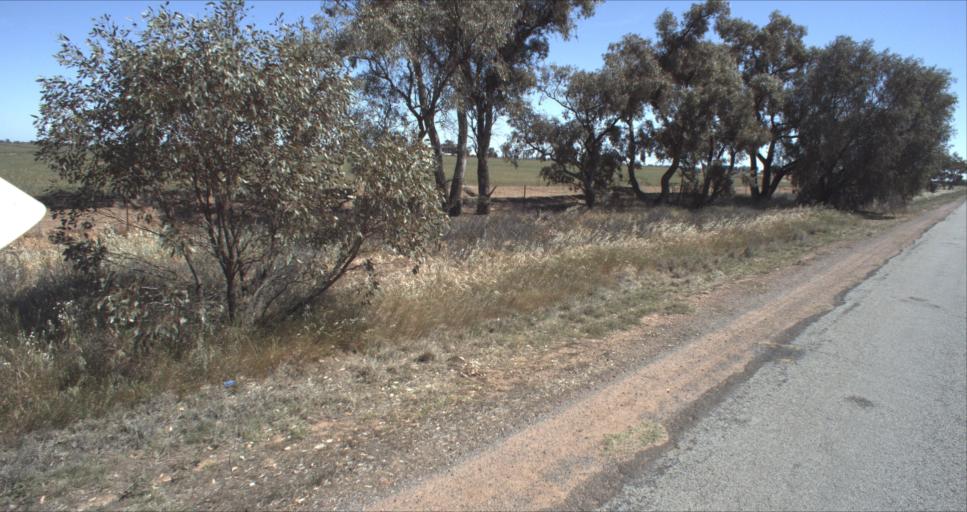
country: AU
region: New South Wales
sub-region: Leeton
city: Leeton
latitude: -34.5564
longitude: 146.3136
